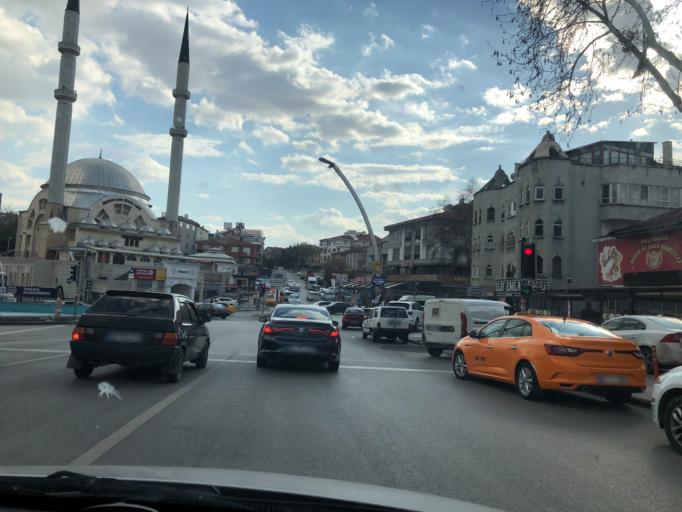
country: TR
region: Ankara
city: Mamak
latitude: 39.9849
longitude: 32.8635
